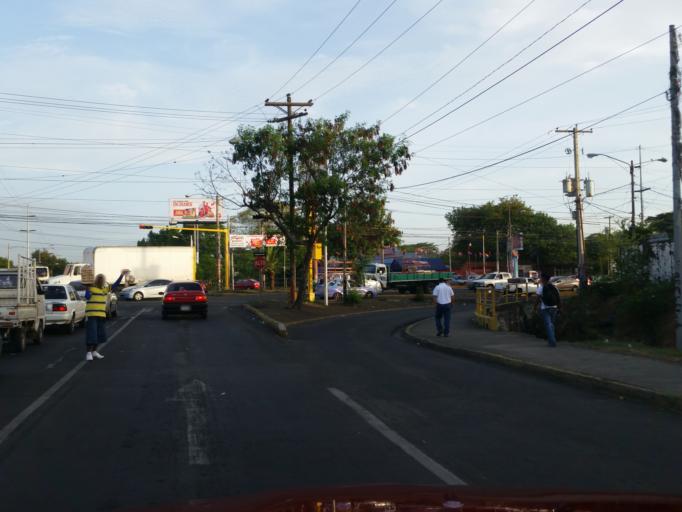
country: NI
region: Managua
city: Managua
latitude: 12.1252
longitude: -86.2749
